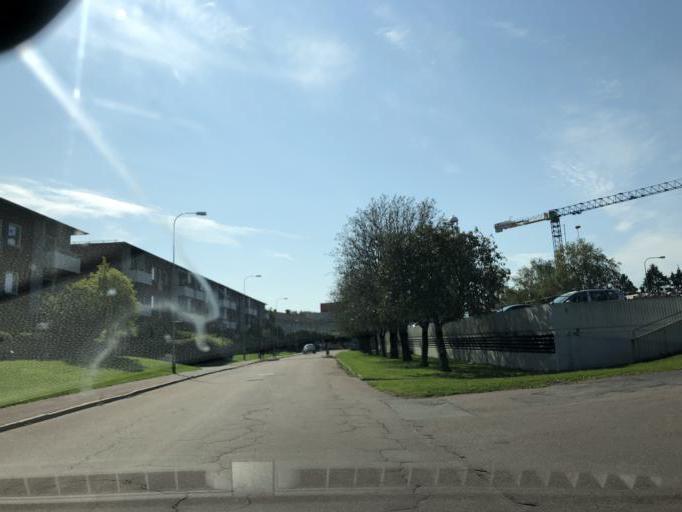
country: SE
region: Vaestra Goetaland
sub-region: Goteborg
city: Goeteborg
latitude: 57.7522
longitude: 11.9819
